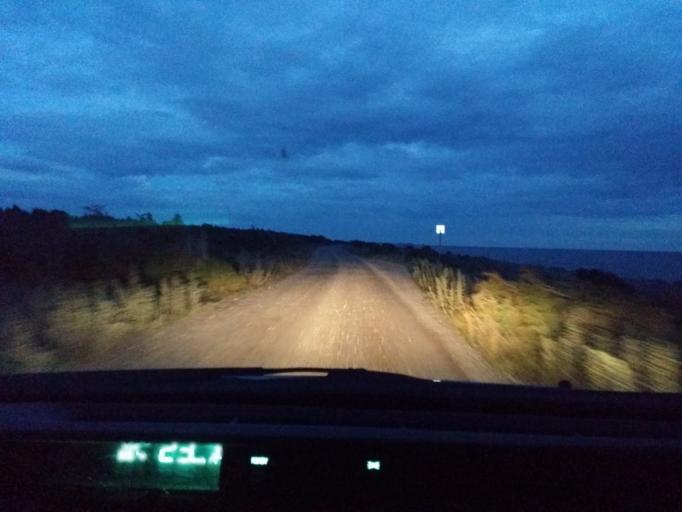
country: SE
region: Kalmar
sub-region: Borgholms Kommun
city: Borgholm
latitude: 57.1422
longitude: 16.9074
